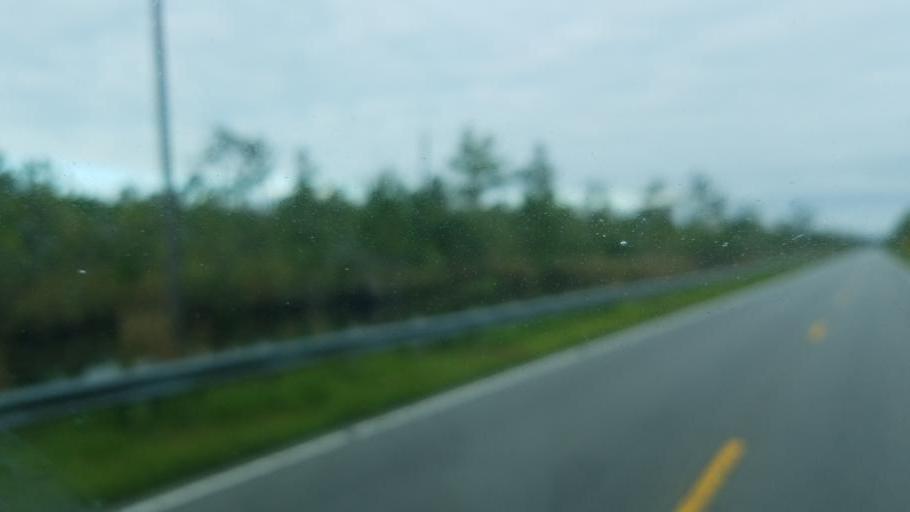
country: US
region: North Carolina
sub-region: Tyrrell County
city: Columbia
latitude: 35.9060
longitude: -76.0448
